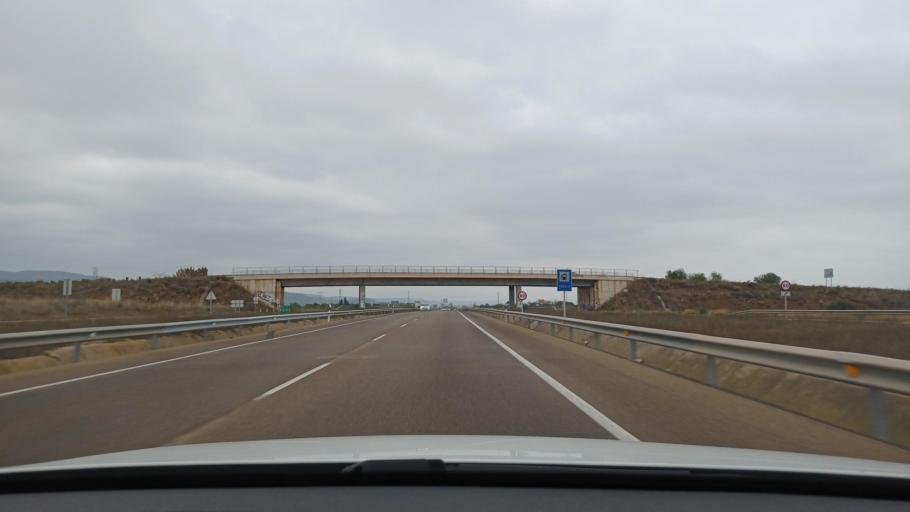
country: ES
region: Valencia
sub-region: Provincia de Castello
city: Orpesa/Oropesa del Mar
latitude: 40.1256
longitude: 0.1450
